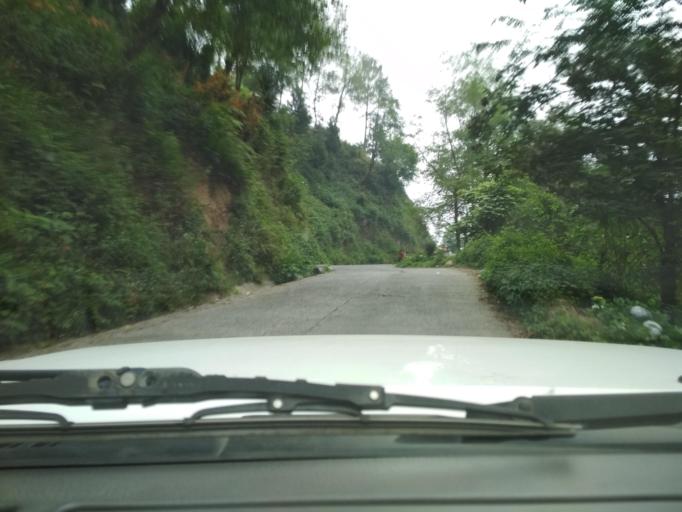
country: MX
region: Veracruz
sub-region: La Perla
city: Metlac Hernandez (Metlac Primero)
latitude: 18.9720
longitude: -97.1464
